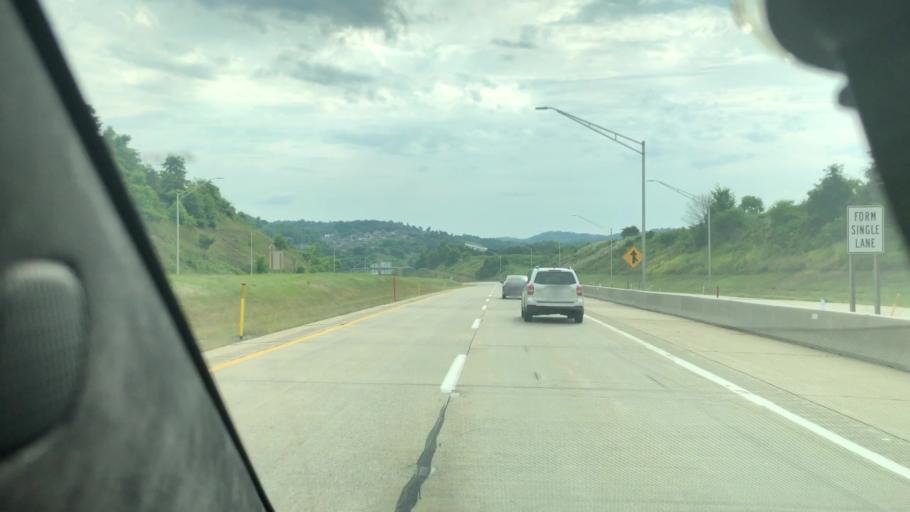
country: US
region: Pennsylvania
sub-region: Allegheny County
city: Jefferson Hills
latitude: 40.2822
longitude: -79.9277
